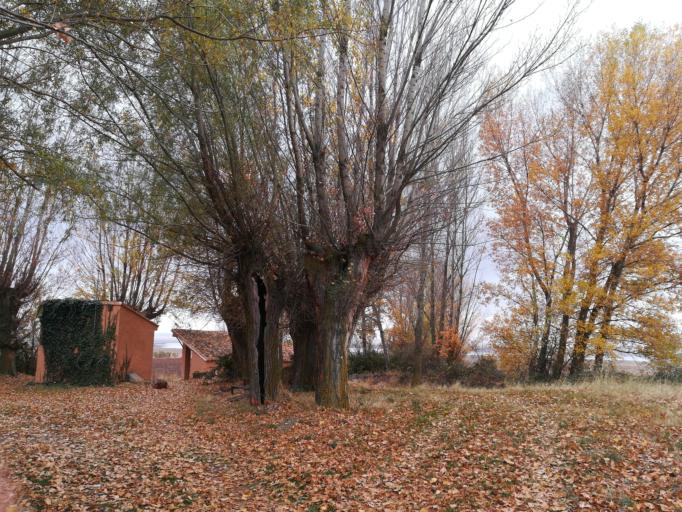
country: ES
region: Aragon
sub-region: Provincia de Teruel
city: Tornos
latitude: 40.9766
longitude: -1.4699
